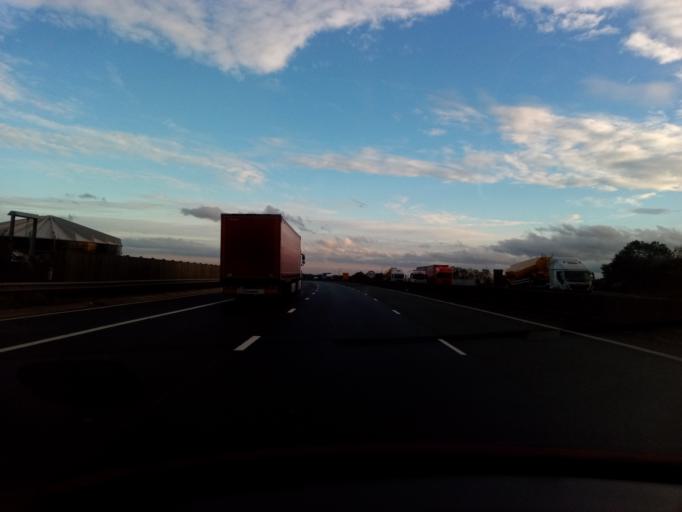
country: GB
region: England
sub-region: North Yorkshire
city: Bedale
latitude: 54.3024
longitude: -1.5684
